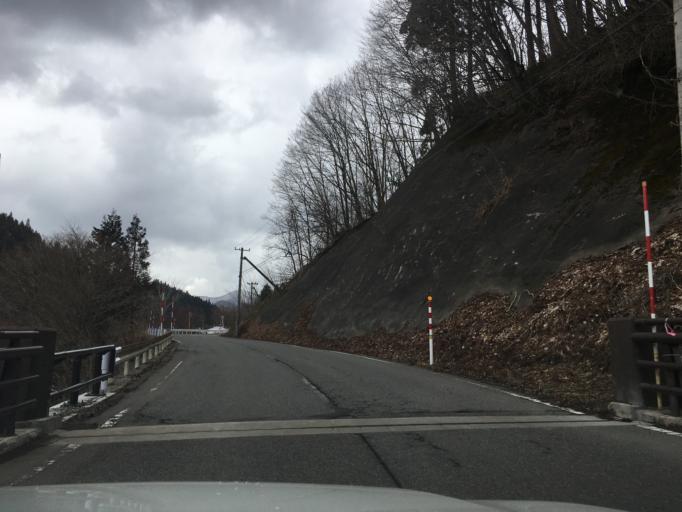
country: JP
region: Akita
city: Odate
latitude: 40.4262
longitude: 140.6547
